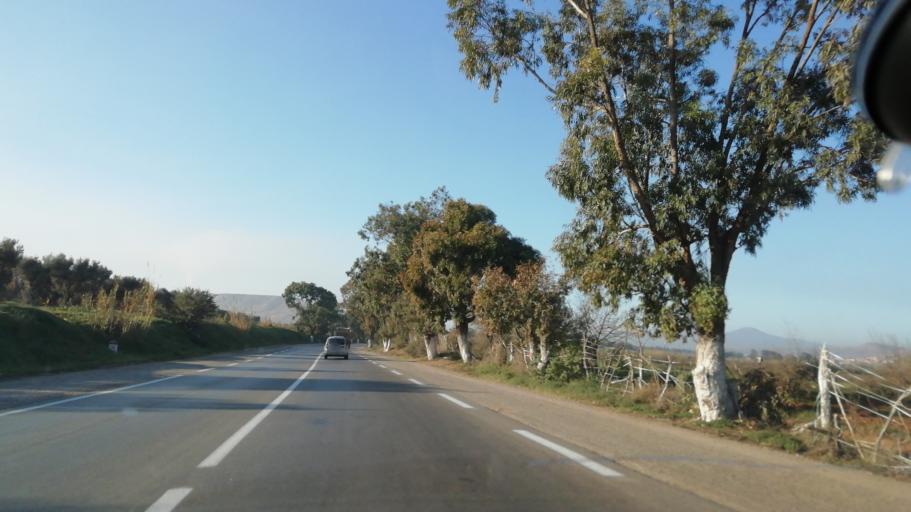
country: DZ
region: Tlemcen
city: Remchi
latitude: 35.0787
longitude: -1.4487
